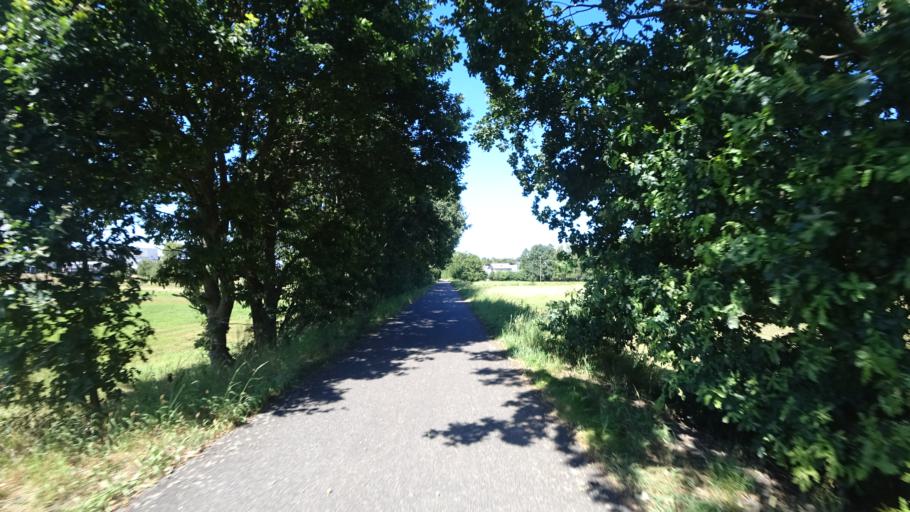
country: DE
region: Rheinland-Pfalz
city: Neuerkirch
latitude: 50.0044
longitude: 7.4976
